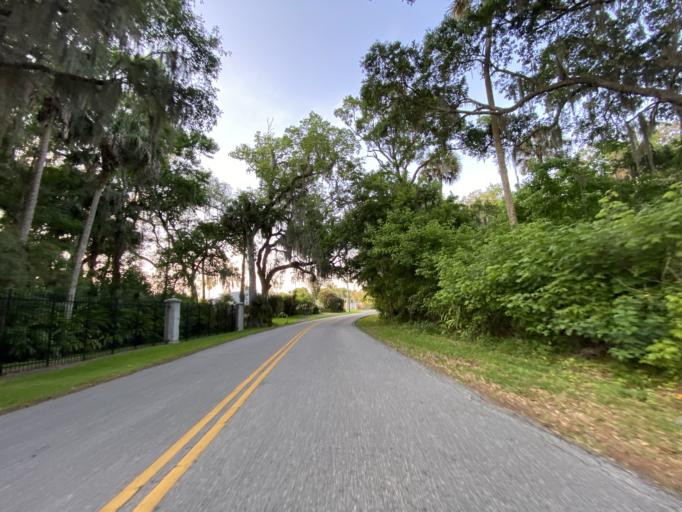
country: US
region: Florida
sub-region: Volusia County
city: Port Orange
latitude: 29.1413
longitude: -81.0055
